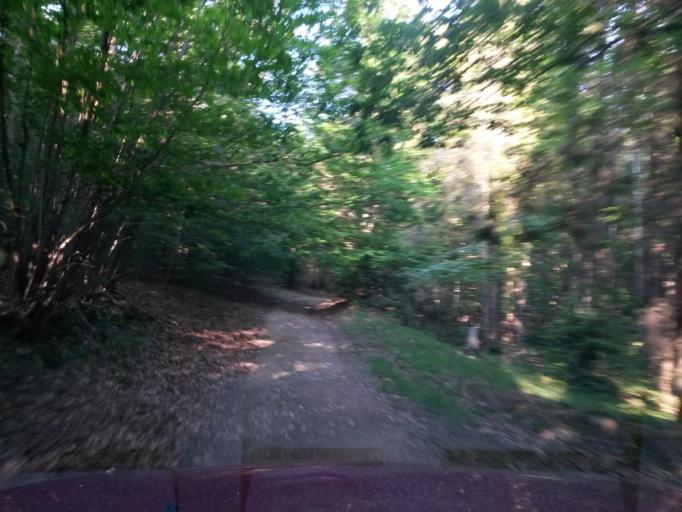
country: SK
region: Kosicky
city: Moldava nad Bodvou
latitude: 48.7404
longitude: 21.0341
